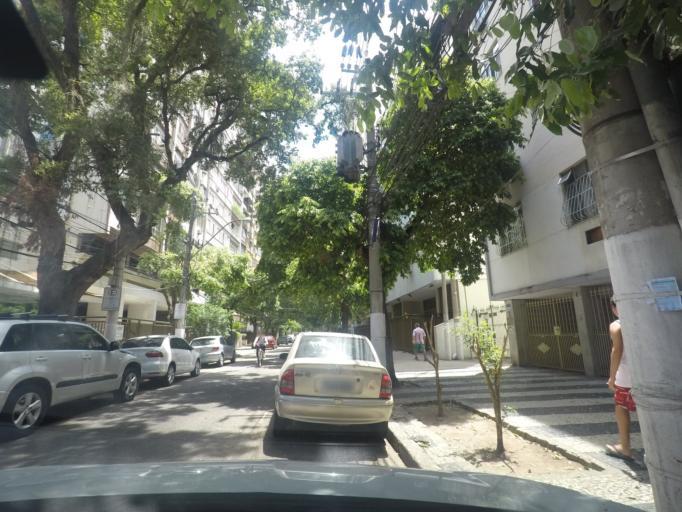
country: BR
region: Rio de Janeiro
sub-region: Niteroi
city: Niteroi
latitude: -22.9055
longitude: -43.1087
